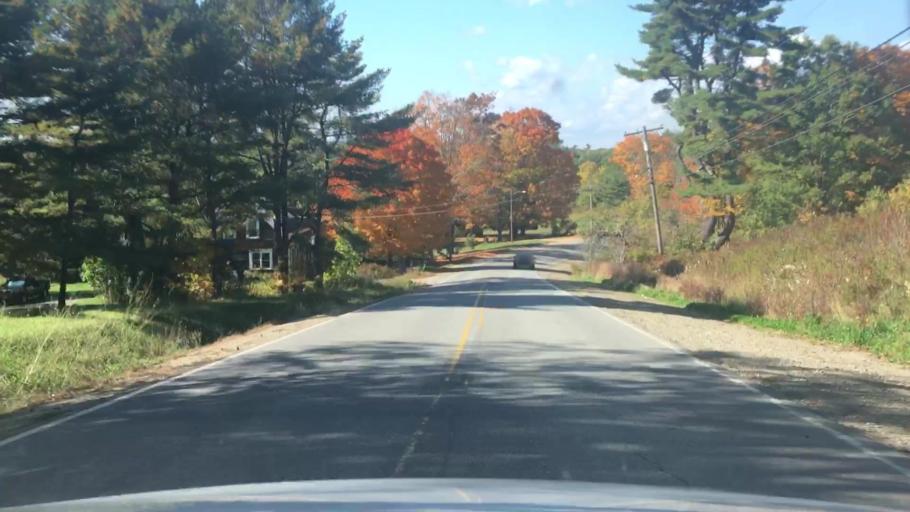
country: US
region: Maine
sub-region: Knox County
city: Thomaston
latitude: 44.0819
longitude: -69.2068
